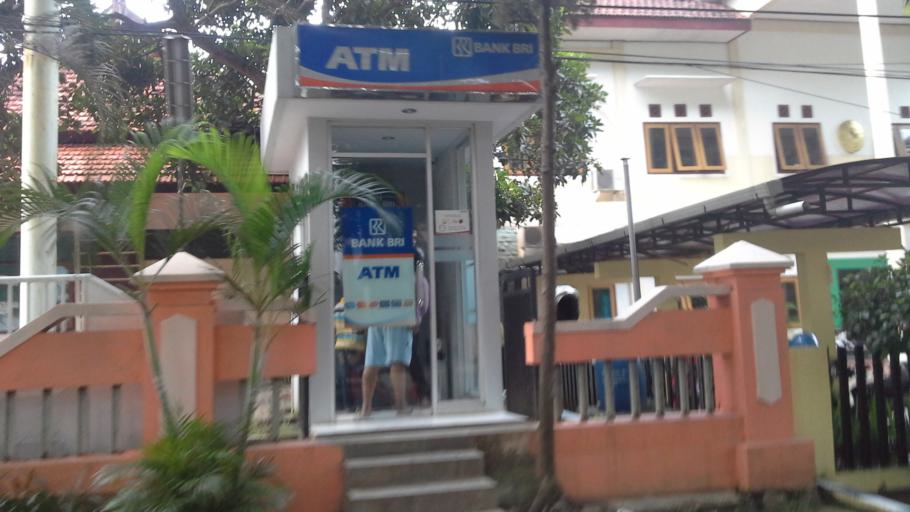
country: ID
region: East Java
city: Bondowoso
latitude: -7.9303
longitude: 113.8175
